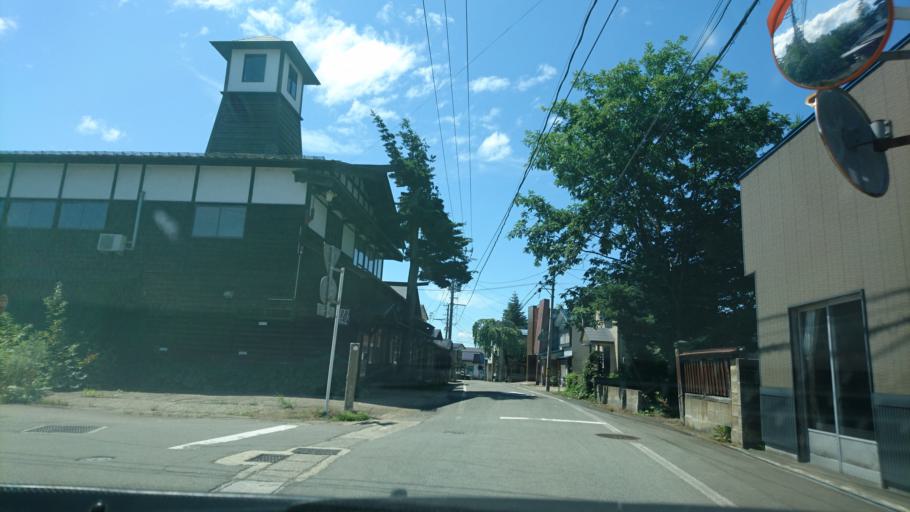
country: JP
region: Akita
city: Kakunodatemachi
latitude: 39.5860
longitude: 140.5637
